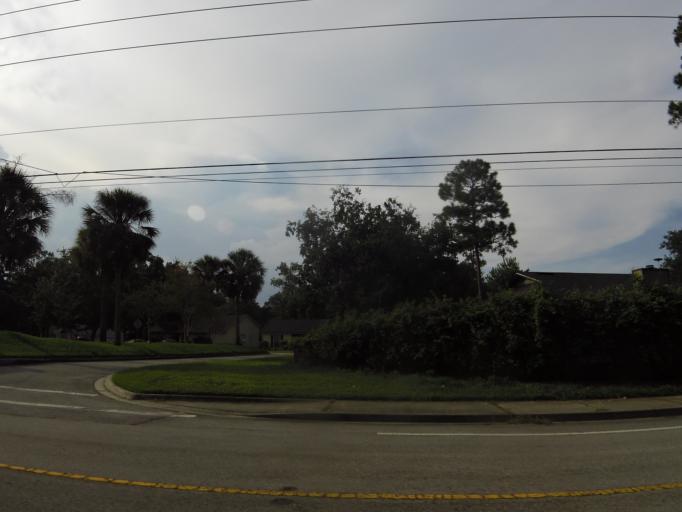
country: US
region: Florida
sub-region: Saint Johns County
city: Fruit Cove
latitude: 30.1844
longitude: -81.6028
